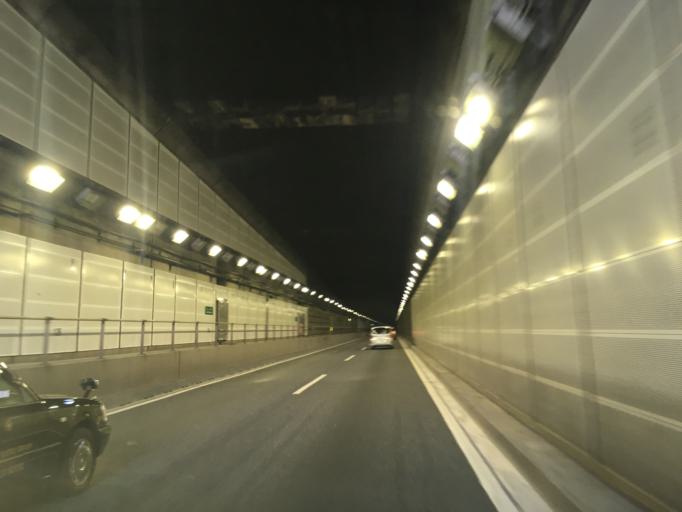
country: JP
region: Saitama
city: Wako
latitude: 35.7302
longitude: 139.6146
